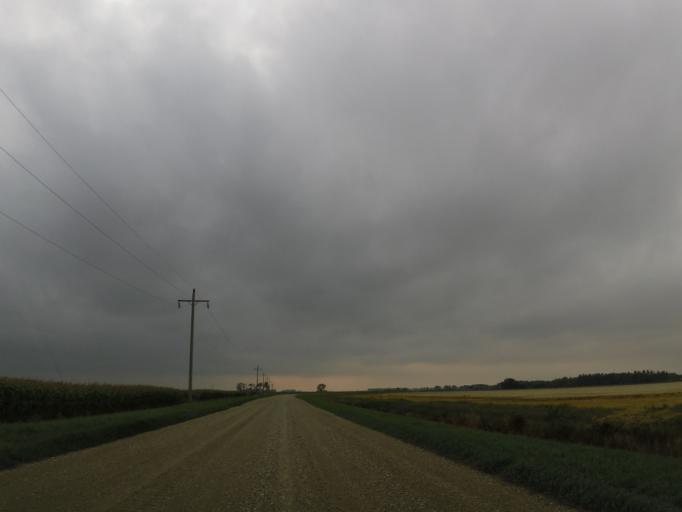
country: US
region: North Dakota
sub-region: Walsh County
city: Grafton
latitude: 48.5284
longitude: -97.1742
